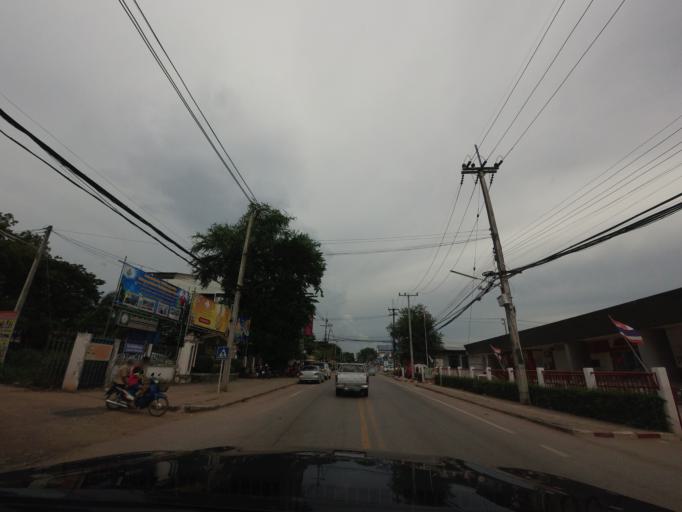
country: TH
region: Changwat Nong Bua Lamphu
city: Si Bun Rueang
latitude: 16.9656
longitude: 102.2752
